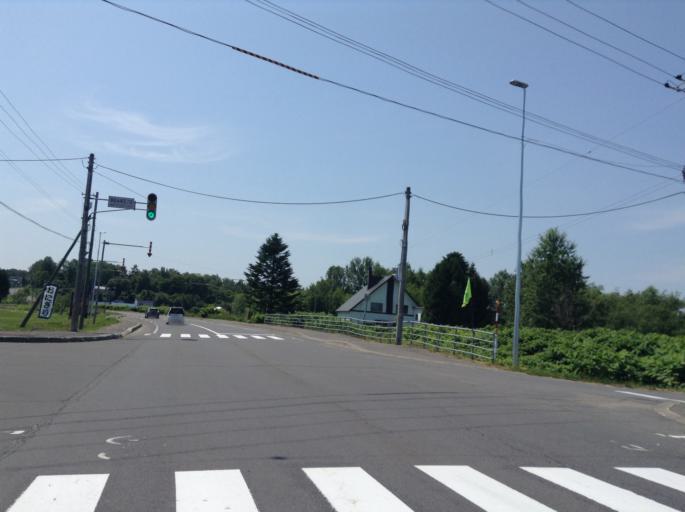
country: JP
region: Hokkaido
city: Nayoro
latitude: 44.3517
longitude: 142.4733
